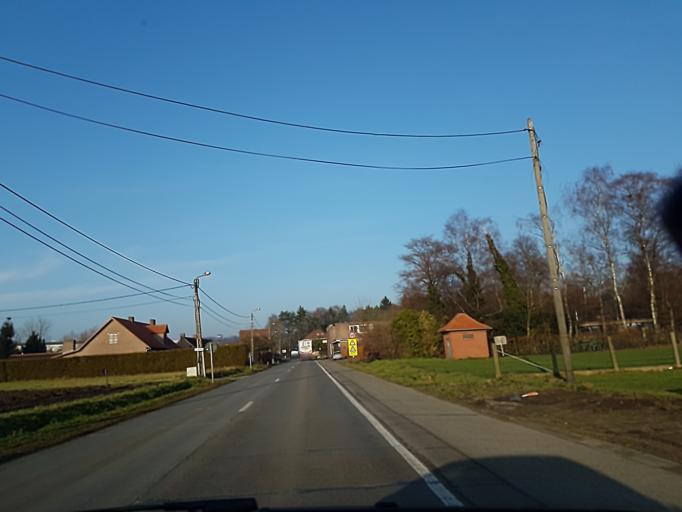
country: BE
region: Flanders
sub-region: Provincie Antwerpen
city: Heist-op-den-Berg
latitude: 51.0651
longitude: 4.7363
